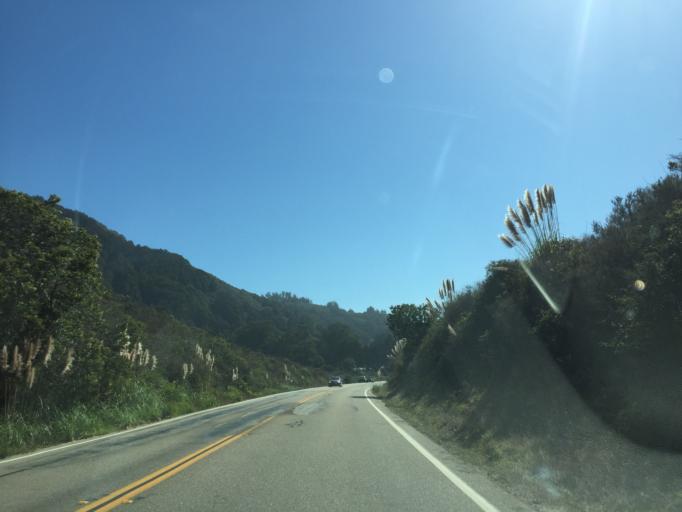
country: US
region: California
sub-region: Monterey County
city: King City
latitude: 35.9242
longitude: -121.4661
